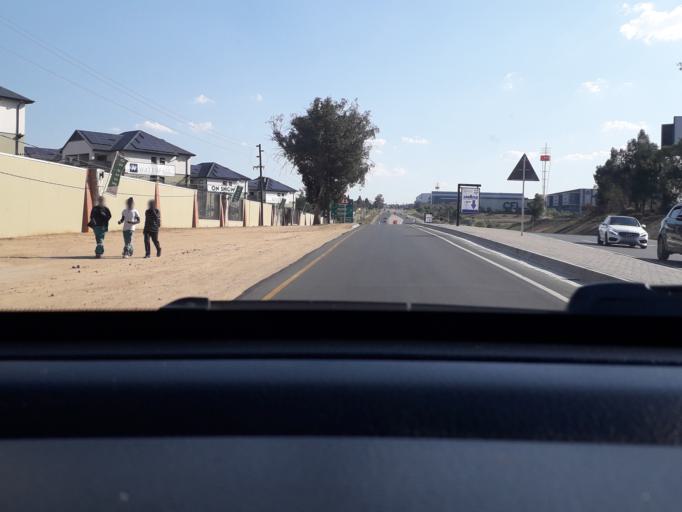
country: ZA
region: Gauteng
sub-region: City of Johannesburg Metropolitan Municipality
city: Midrand
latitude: -26.0400
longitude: 28.1069
